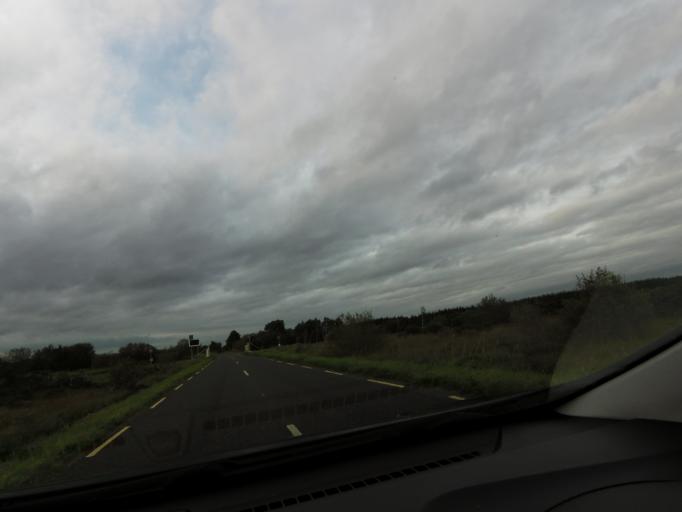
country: IE
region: Leinster
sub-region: Uibh Fhaili
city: Ferbane
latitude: 53.2100
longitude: -7.7878
